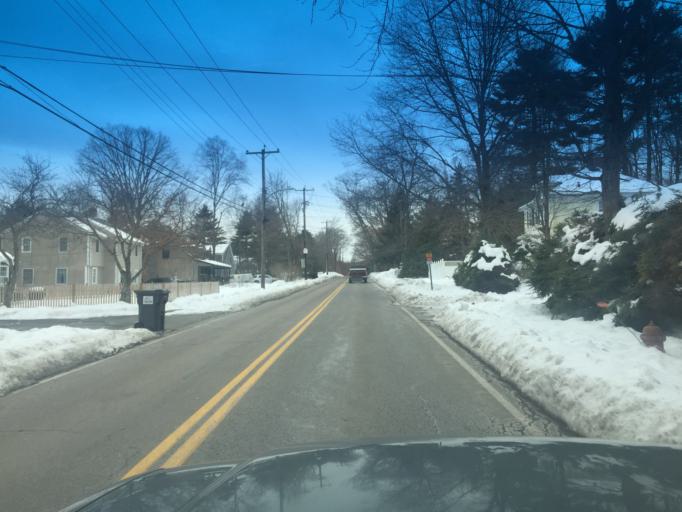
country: US
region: Massachusetts
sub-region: Norfolk County
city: Millis
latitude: 42.1596
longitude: -71.3649
